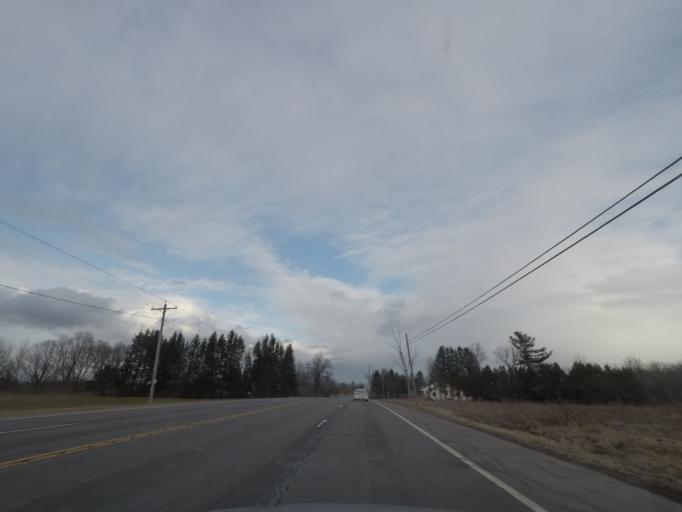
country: US
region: New York
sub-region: Oneida County
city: Clark Mills
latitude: 43.0802
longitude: -75.4170
